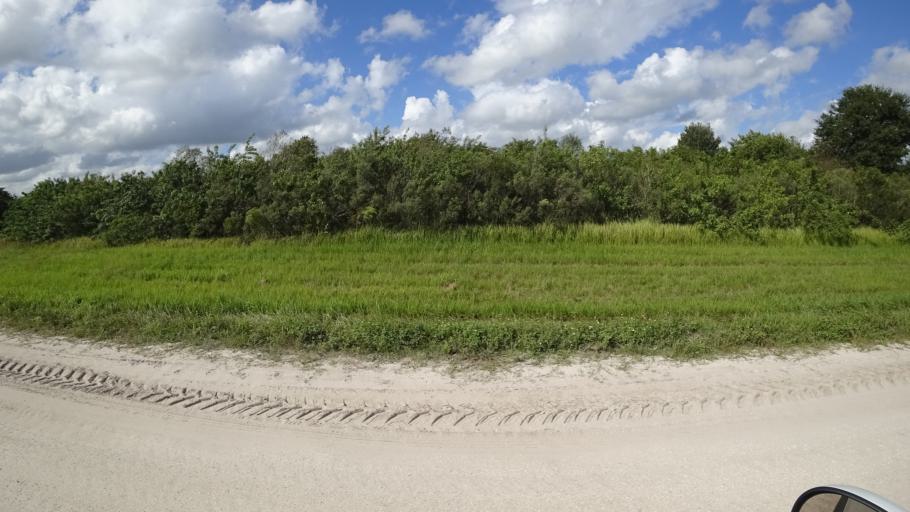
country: US
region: Florida
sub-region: Sarasota County
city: Lake Sarasota
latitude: 27.4411
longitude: -82.1826
